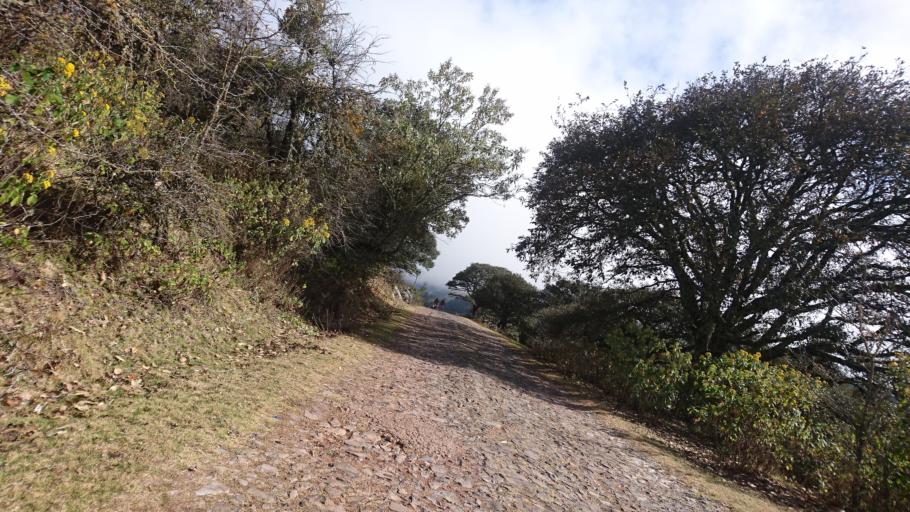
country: MX
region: San Luis Potosi
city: Zaragoza
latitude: 22.0662
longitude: -100.6434
